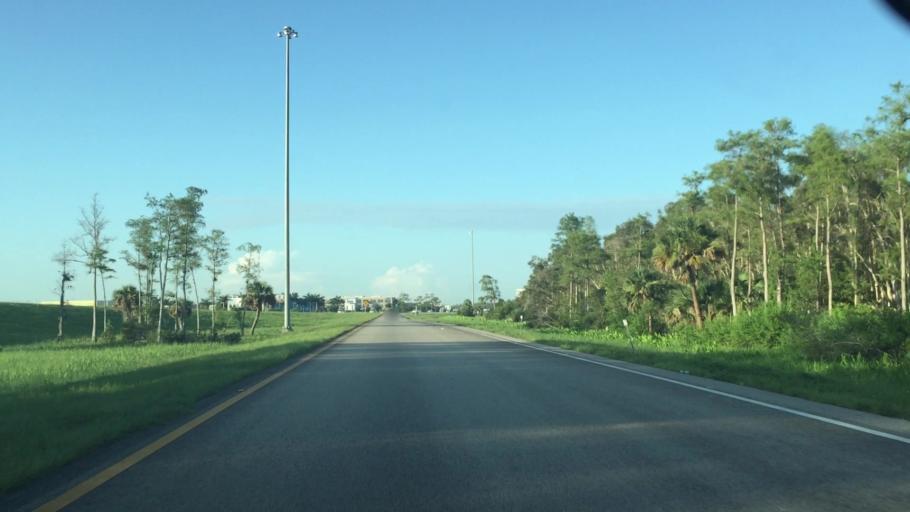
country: US
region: Florida
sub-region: Lee County
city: Fort Myers
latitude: 26.6340
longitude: -81.8043
